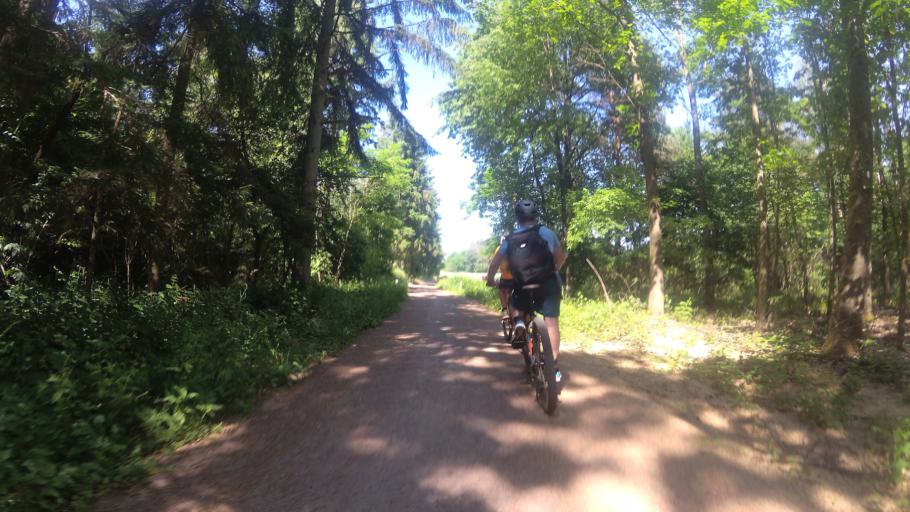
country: DE
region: Saarland
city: Beckingen
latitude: 49.4036
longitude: 6.7400
